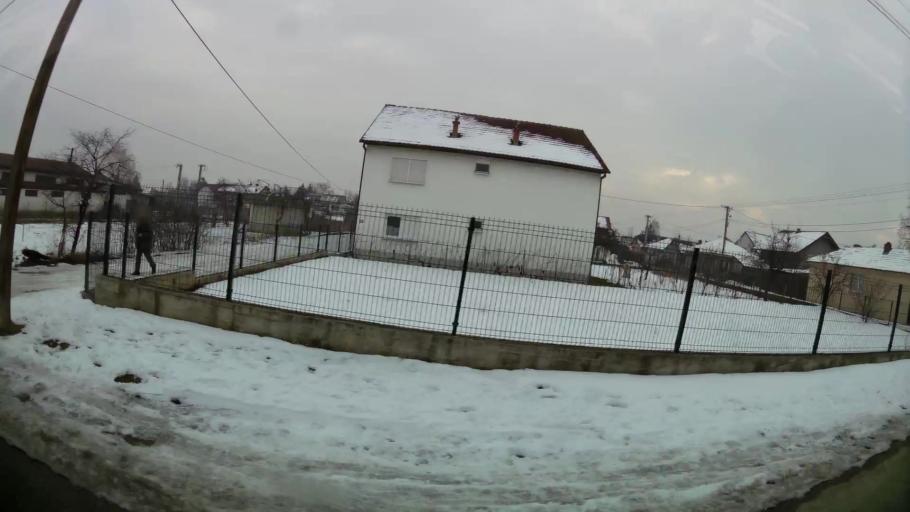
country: MK
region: Saraj
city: Saraj
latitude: 42.0460
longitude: 21.3539
